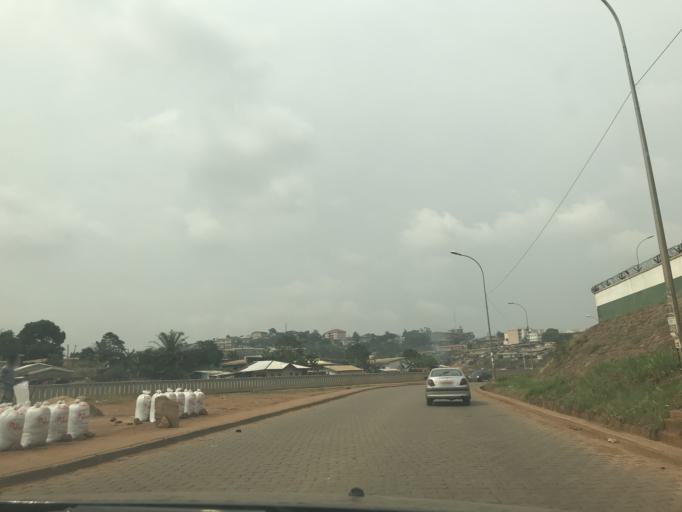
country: CM
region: Centre
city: Yaounde
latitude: 3.8304
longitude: 11.5145
